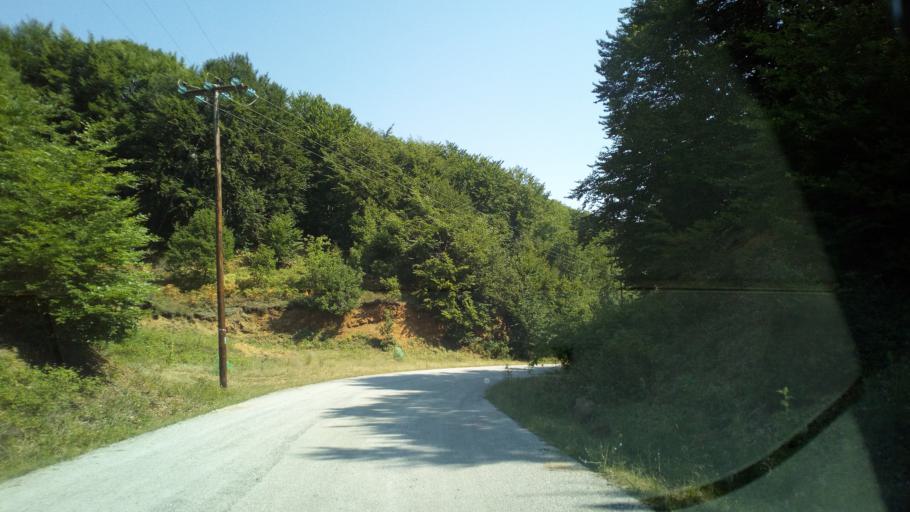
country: GR
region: Central Macedonia
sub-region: Nomos Thessalonikis
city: Sochos
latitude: 40.8272
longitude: 23.3447
